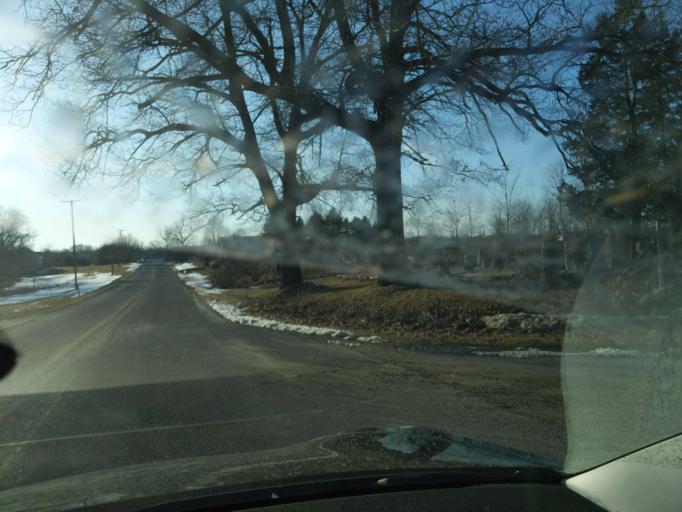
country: US
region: Michigan
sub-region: Ingham County
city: Stockbridge
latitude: 42.5194
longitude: -84.2396
